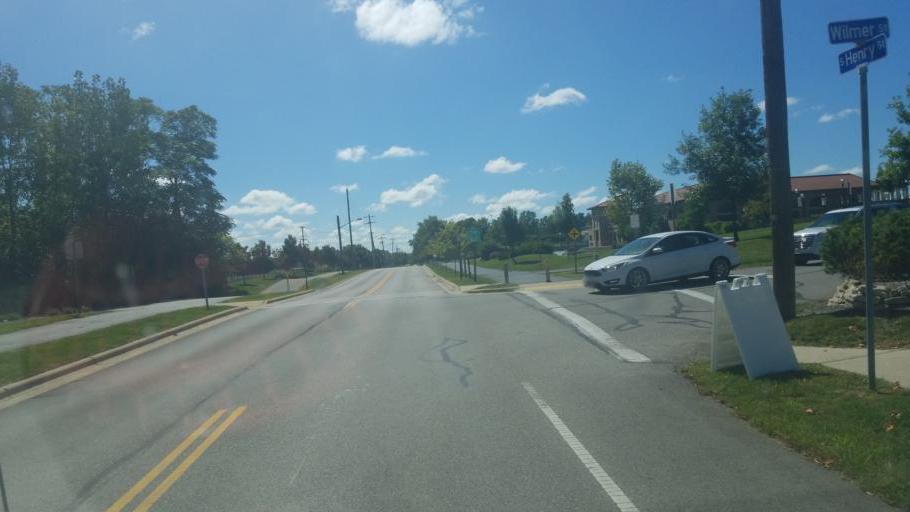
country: US
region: Ohio
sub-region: Delaware County
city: Delaware
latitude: 40.2948
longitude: -83.0646
